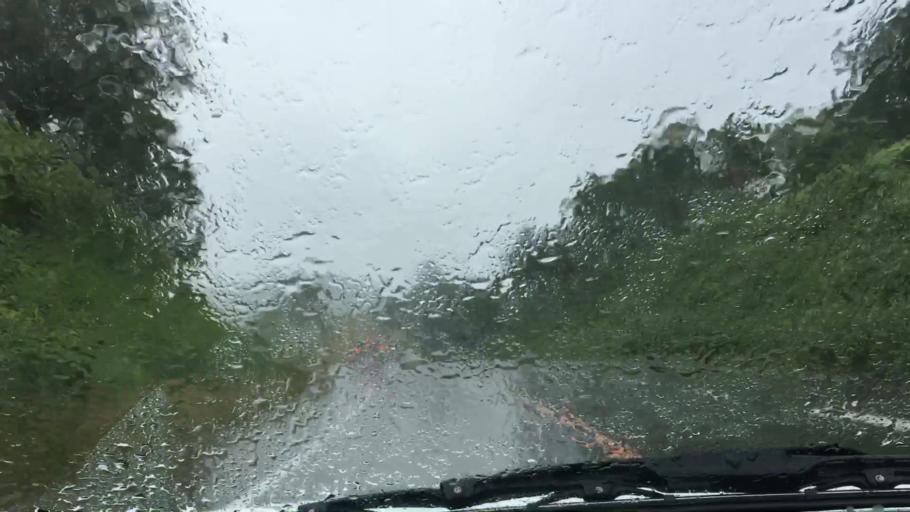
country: JP
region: Hokkaido
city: Sapporo
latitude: 42.8490
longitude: 141.0841
